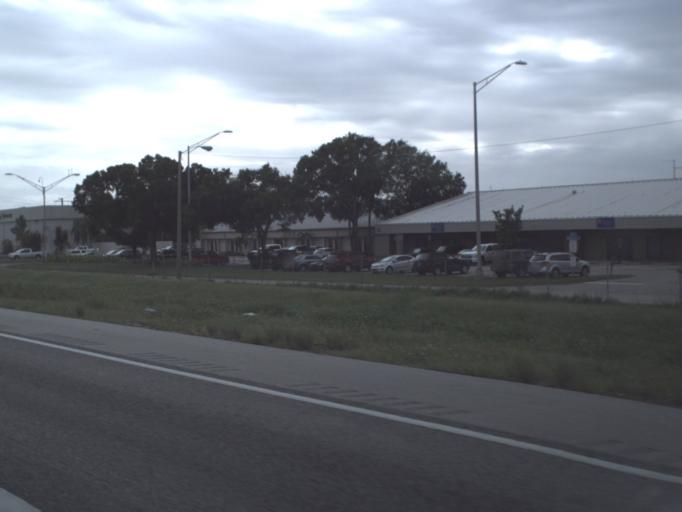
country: US
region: Florida
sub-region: Lee County
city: Tice
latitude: 26.6649
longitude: -81.7999
